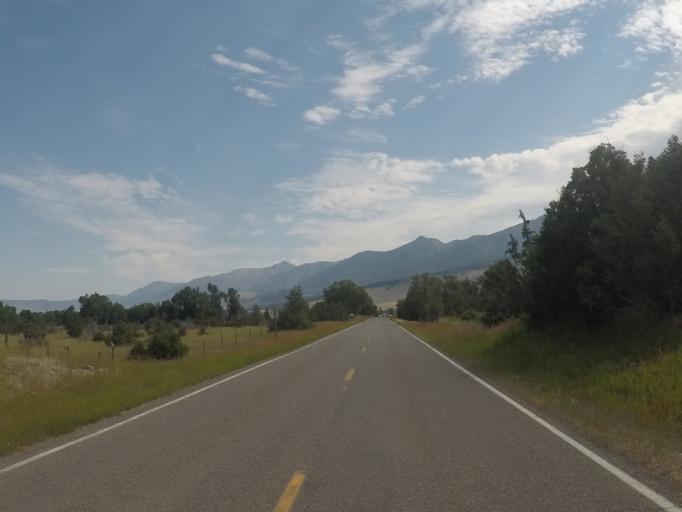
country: US
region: Montana
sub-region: Park County
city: Livingston
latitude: 45.4181
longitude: -110.6378
